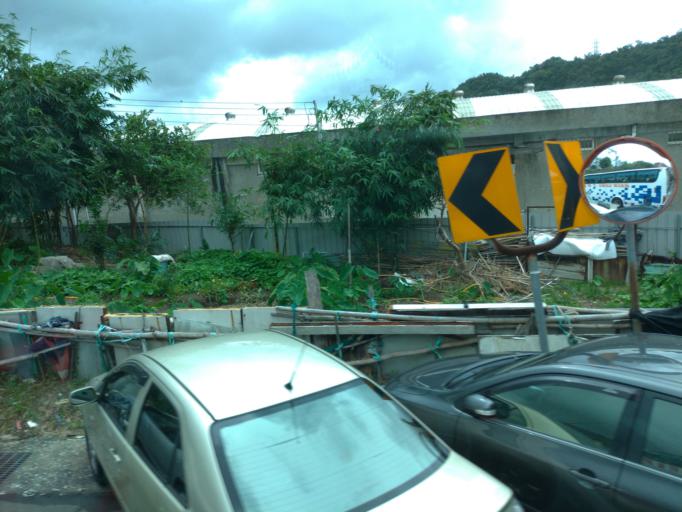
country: TW
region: Taiwan
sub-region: Keelung
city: Keelung
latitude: 25.0974
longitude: 121.7488
